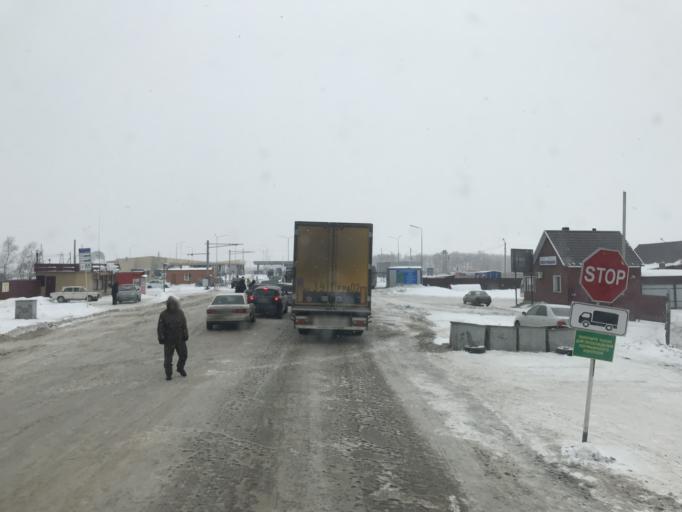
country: RU
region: Kurgan
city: Petukhovo
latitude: 55.0942
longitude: 68.2798
